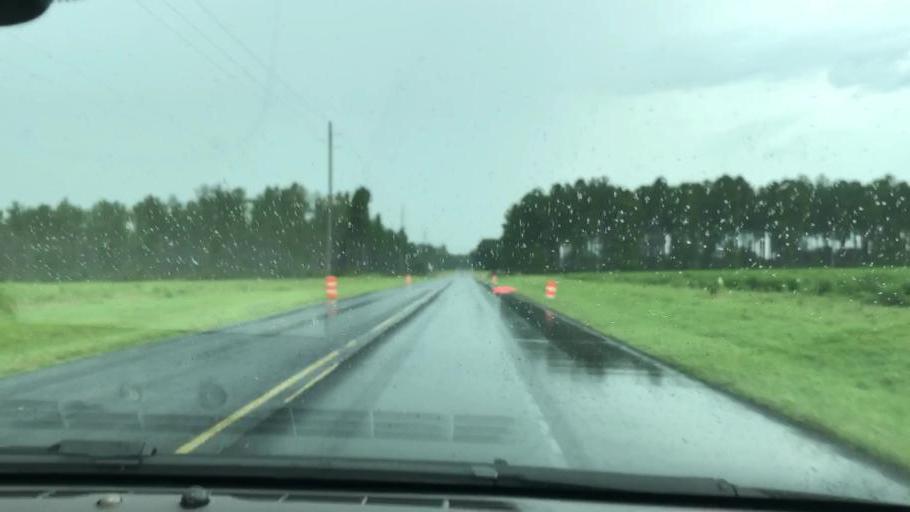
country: US
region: Georgia
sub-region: Clay County
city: Fort Gaines
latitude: 31.5316
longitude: -85.0216
